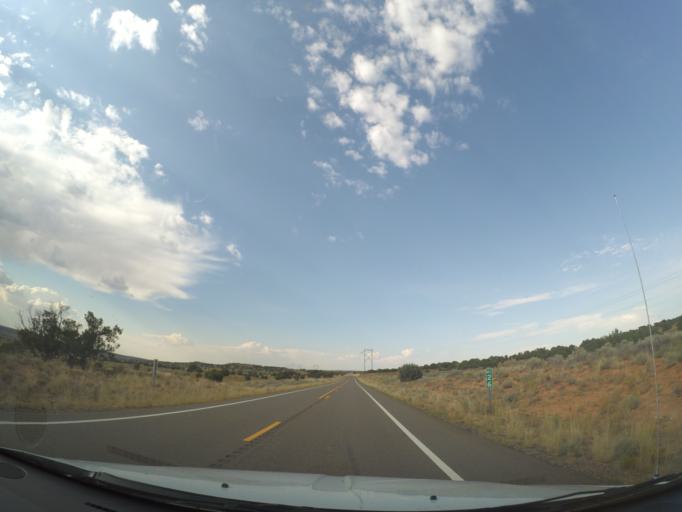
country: US
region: Arizona
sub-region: Coconino County
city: LeChee
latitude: 36.6450
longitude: -111.4395
